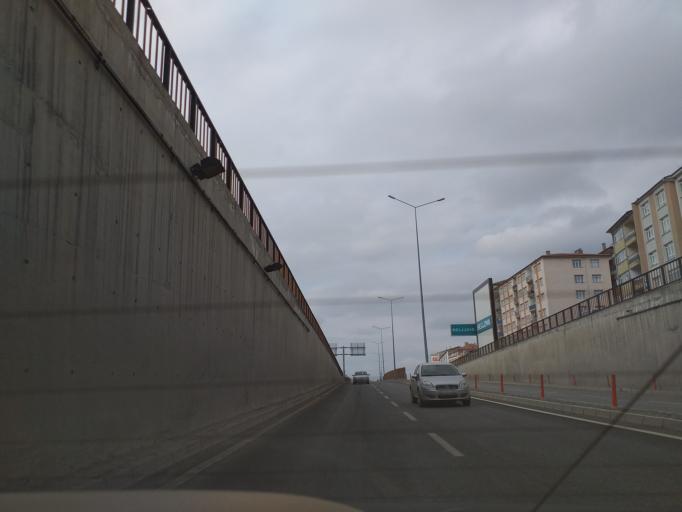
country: TR
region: Yozgat
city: Yozgat
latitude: 39.8207
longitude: 34.8080
